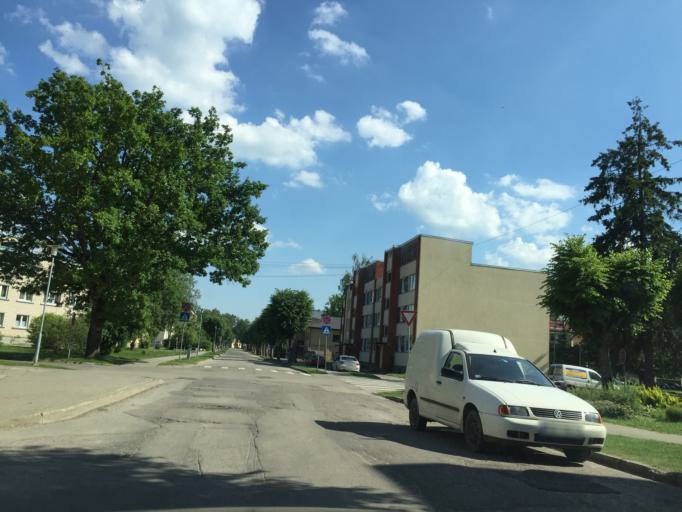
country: LV
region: Sigulda
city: Sigulda
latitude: 57.1597
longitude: 24.8469
